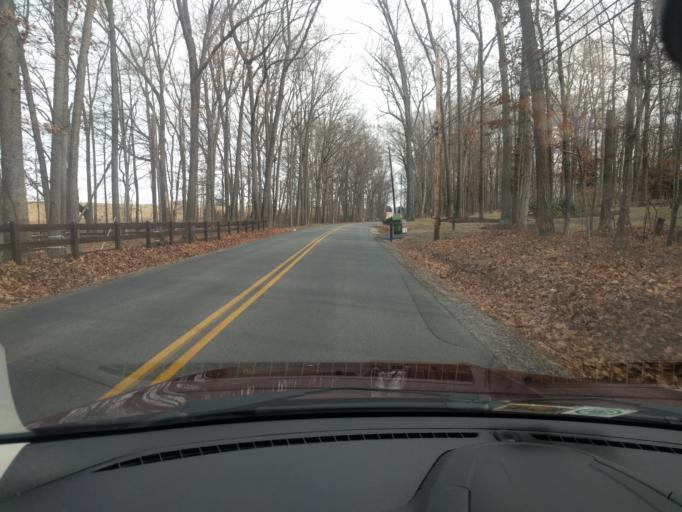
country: US
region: Virginia
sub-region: Augusta County
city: Fishersville
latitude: 38.0835
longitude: -78.9566
